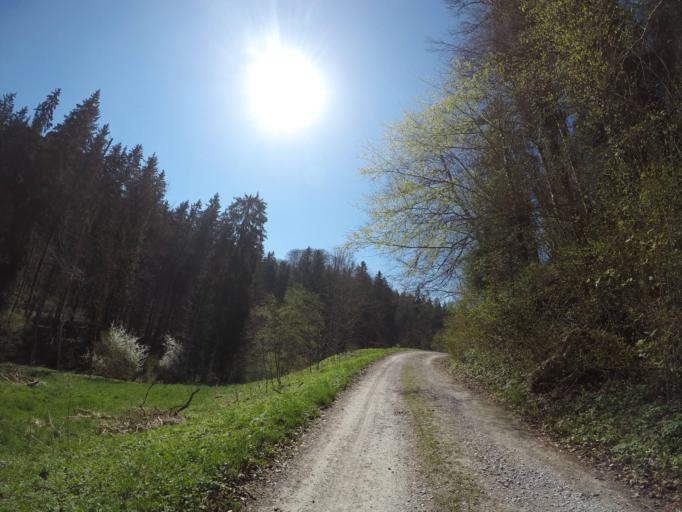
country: DE
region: Baden-Wuerttemberg
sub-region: Tuebingen Region
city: Horgenzell
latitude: 47.8127
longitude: 9.4612
